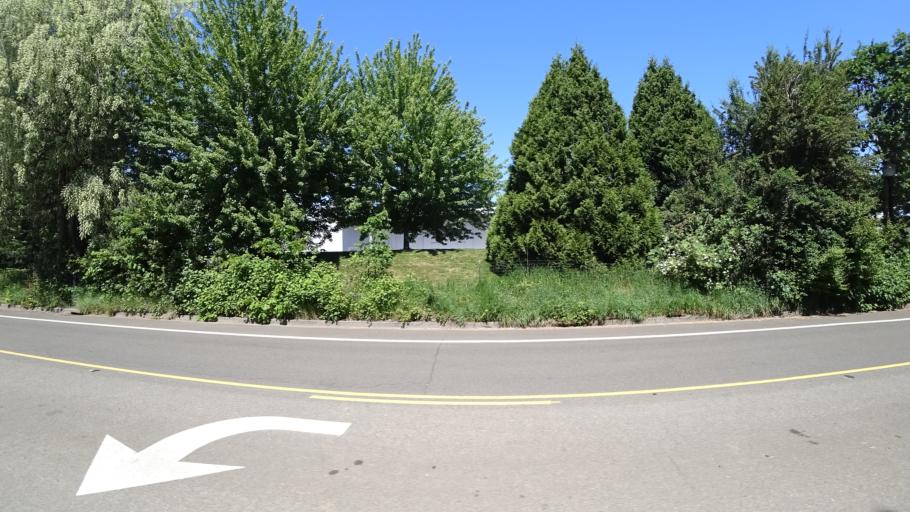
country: US
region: Oregon
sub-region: Washington County
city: Rockcreek
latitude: 45.5310
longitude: -122.9084
